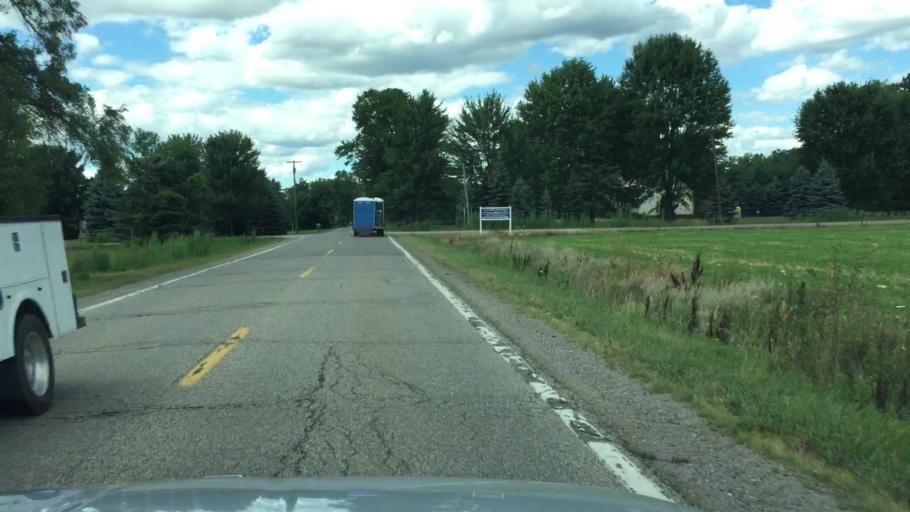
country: US
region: Michigan
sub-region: Macomb County
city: Armada
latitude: 42.8634
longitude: -82.9448
